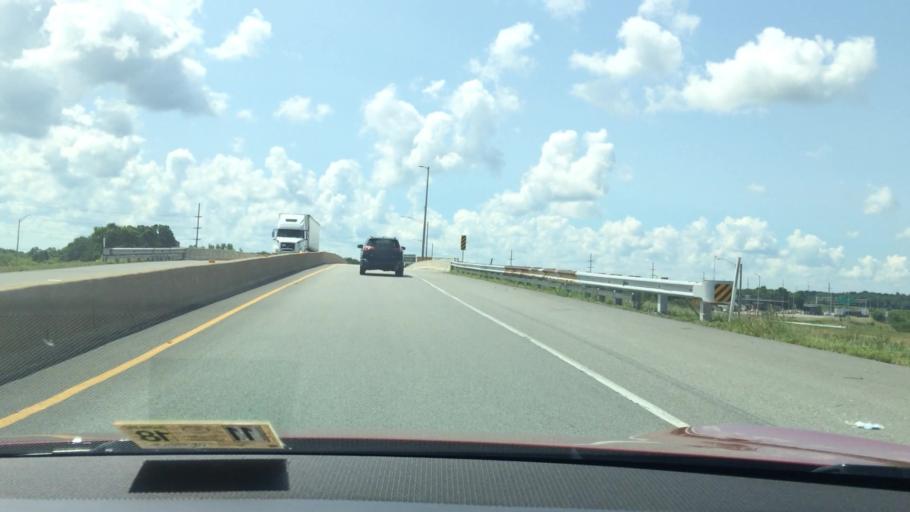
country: US
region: Indiana
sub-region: Saint Joseph County
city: South Bend
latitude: 41.7313
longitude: -86.3335
